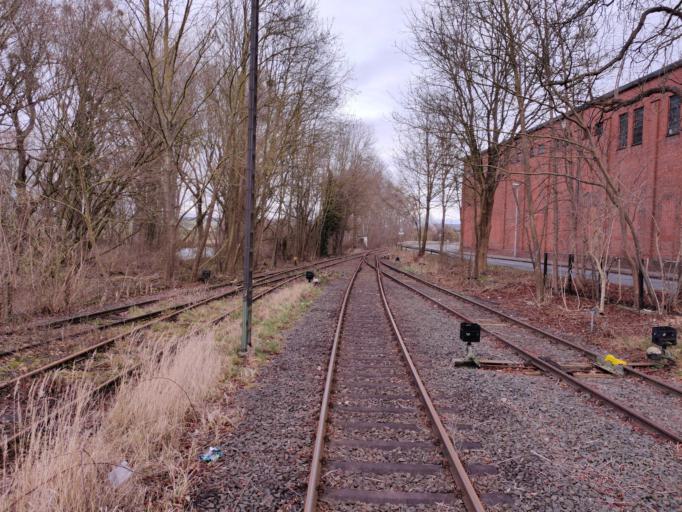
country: DE
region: Lower Saxony
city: Bockenem
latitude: 52.0135
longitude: 10.1230
